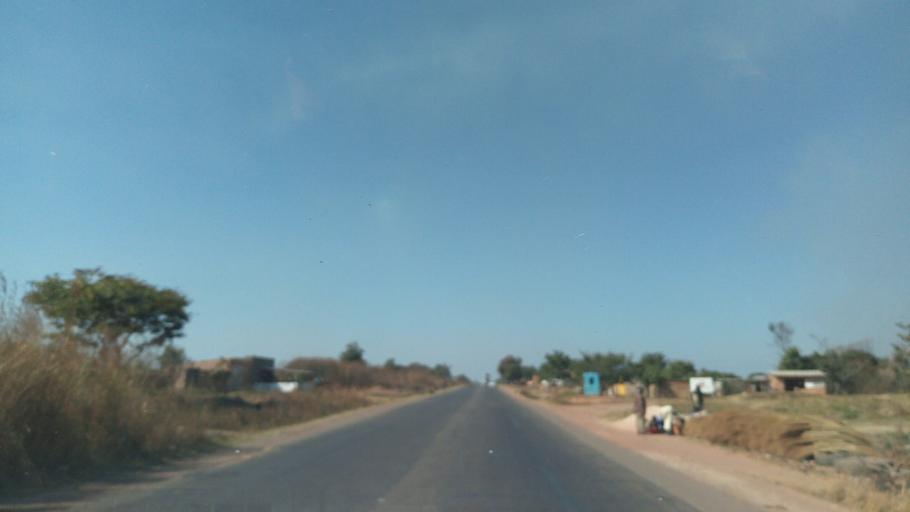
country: CD
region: Katanga
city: Lubumbashi
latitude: -11.5623
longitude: 27.5654
